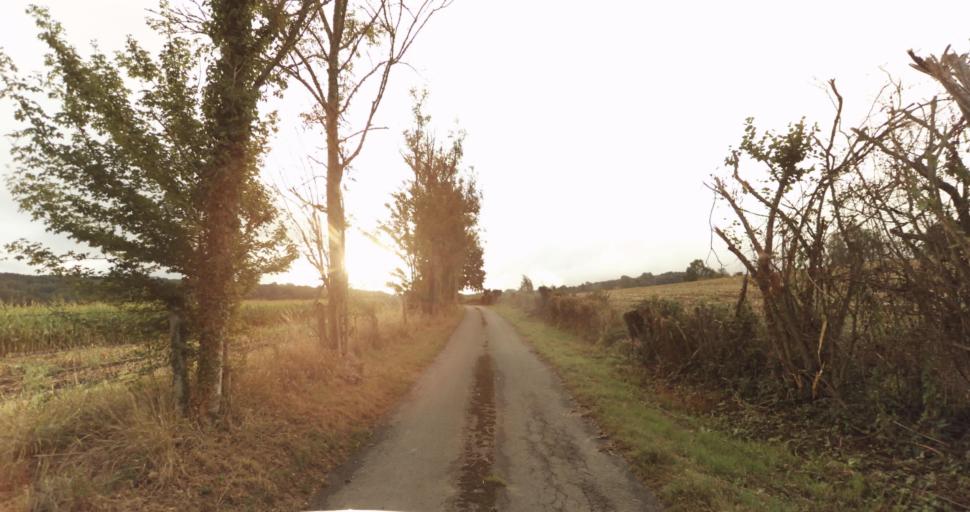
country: FR
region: Lower Normandy
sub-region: Departement de l'Orne
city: Trun
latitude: 48.8984
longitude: 0.0941
